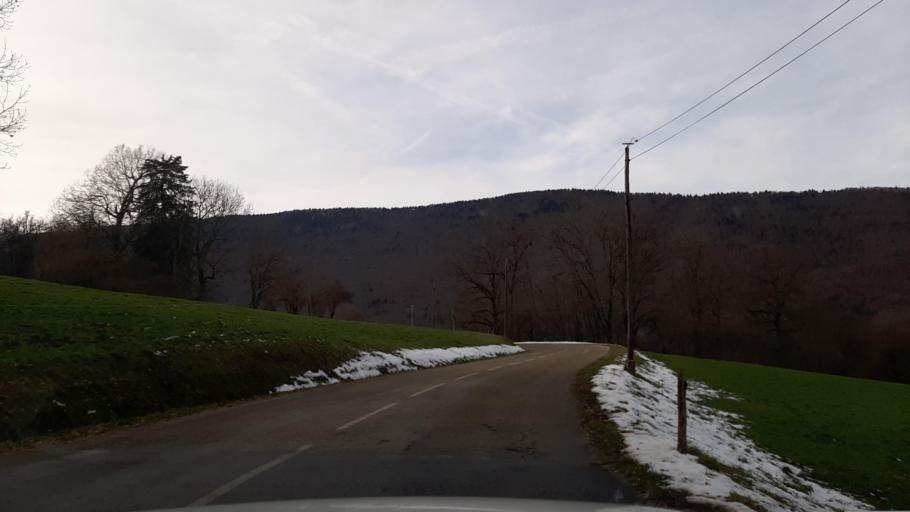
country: FR
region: Rhone-Alpes
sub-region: Departement de la Haute-Savoie
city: Gruffy
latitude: 45.6797
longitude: 6.1186
